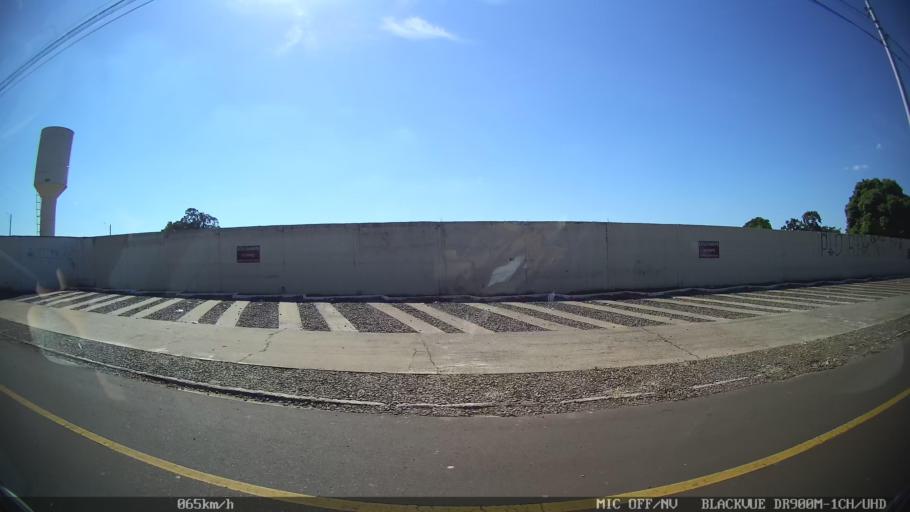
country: BR
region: Sao Paulo
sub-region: Franca
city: Franca
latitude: -20.5478
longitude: -47.4477
